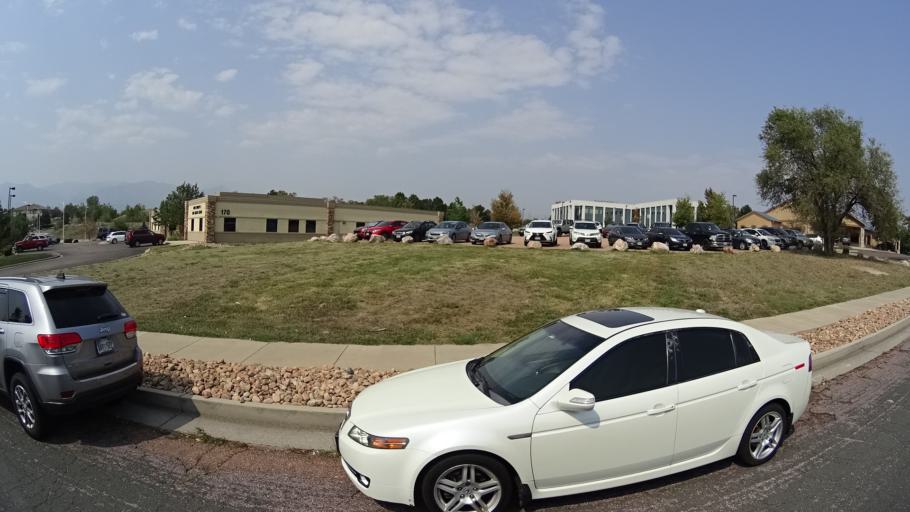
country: US
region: Colorado
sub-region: El Paso County
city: Colorado Springs
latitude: 38.8295
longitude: -104.7858
